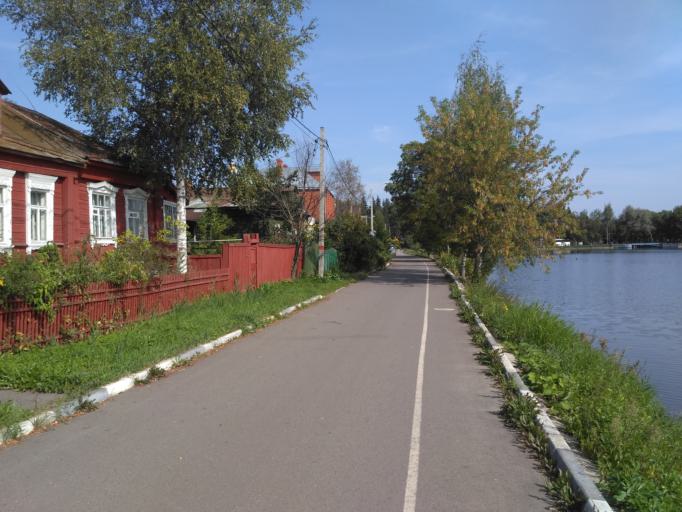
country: RU
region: Moskovskaya
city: Sergiyev Posad
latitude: 56.3047
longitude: 38.1259
